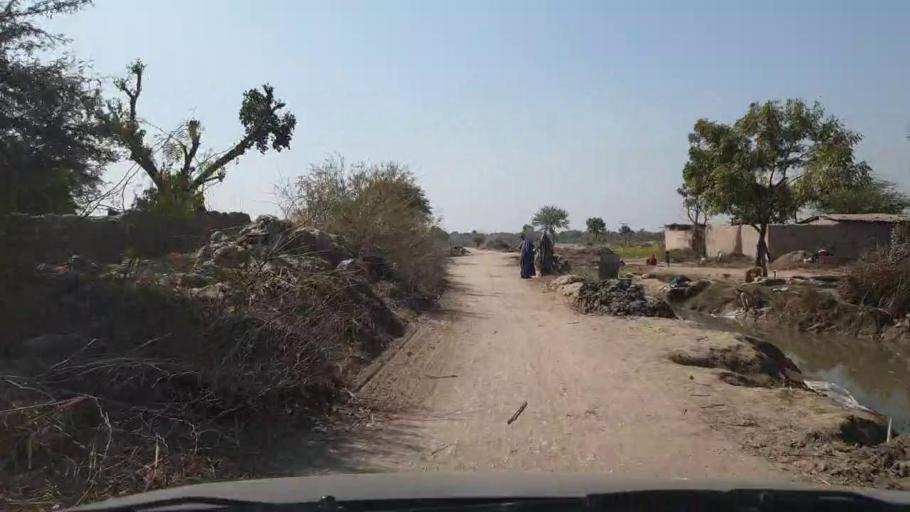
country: PK
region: Sindh
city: Tando Jam
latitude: 25.4242
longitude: 68.6302
